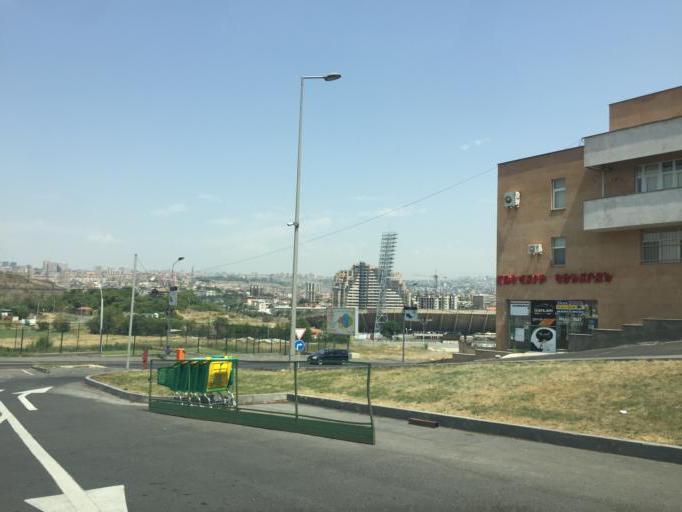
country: AM
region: Yerevan
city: Yerevan
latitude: 40.1796
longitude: 44.4894
